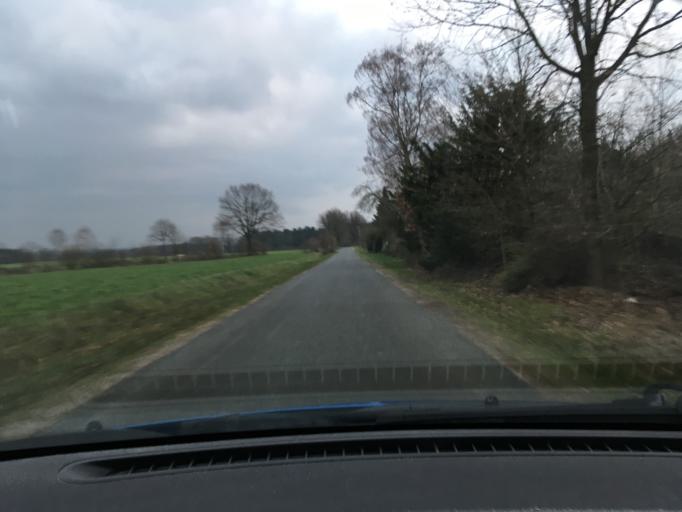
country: DE
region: Lower Saxony
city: Walsrode
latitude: 52.8390
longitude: 9.5638
